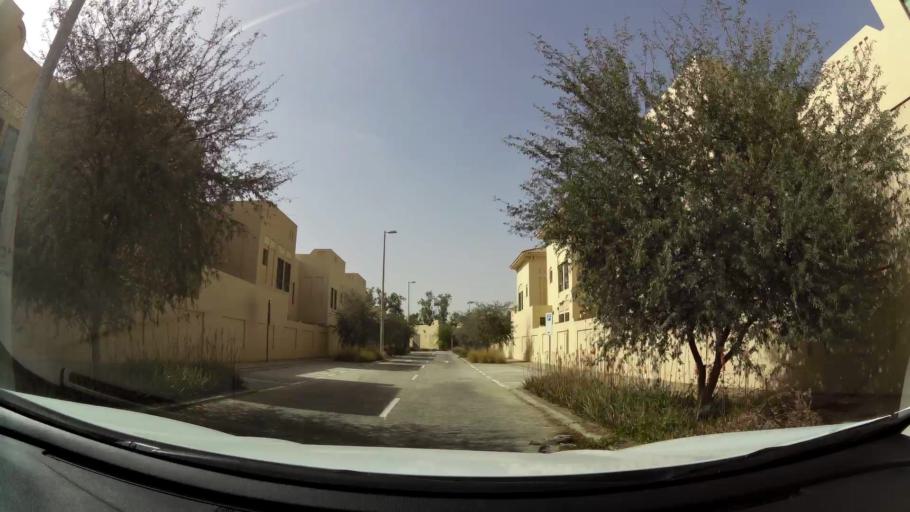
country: AE
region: Abu Dhabi
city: Abu Dhabi
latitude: 24.4099
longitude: 54.5337
